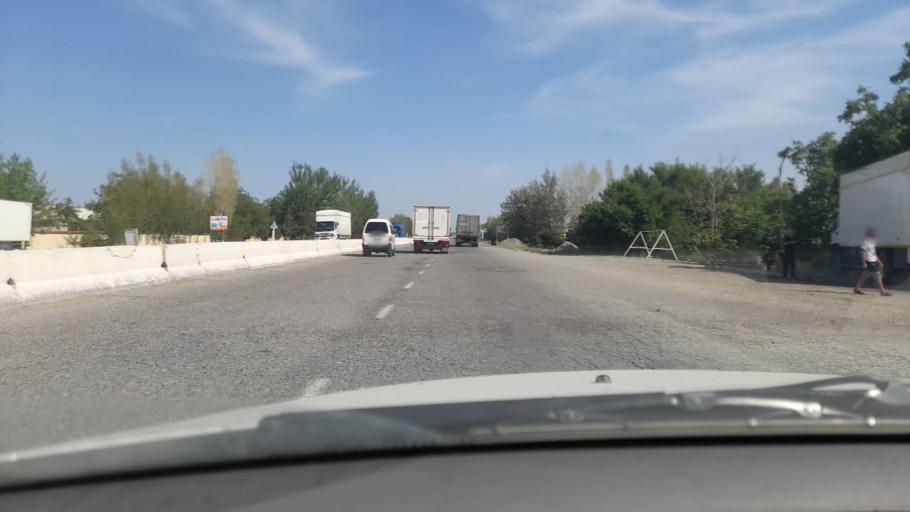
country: UZ
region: Samarqand
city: Chelak
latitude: 39.8525
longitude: 66.7982
